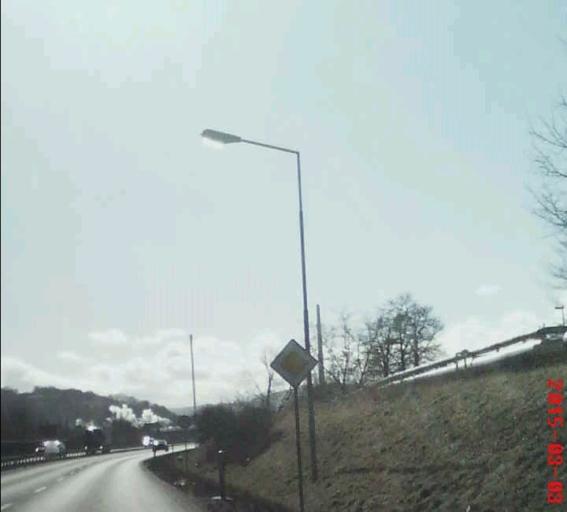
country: DE
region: Thuringia
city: Rudolstadt
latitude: 50.7002
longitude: 11.3252
